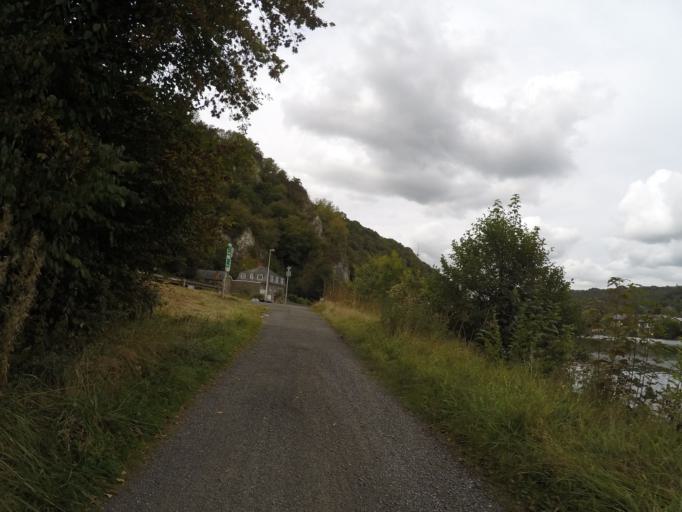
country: BE
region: Wallonia
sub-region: Province de Namur
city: Yvoir
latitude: 50.3253
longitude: 4.8722
